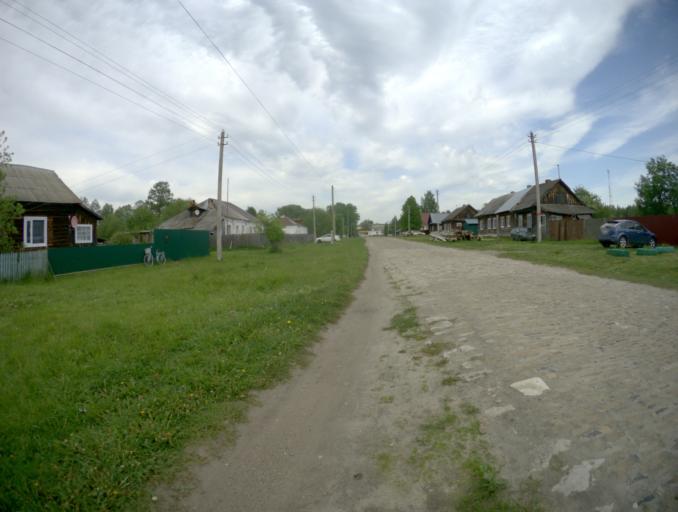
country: RU
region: Vladimir
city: Ivanishchi
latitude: 55.7718
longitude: 40.4209
